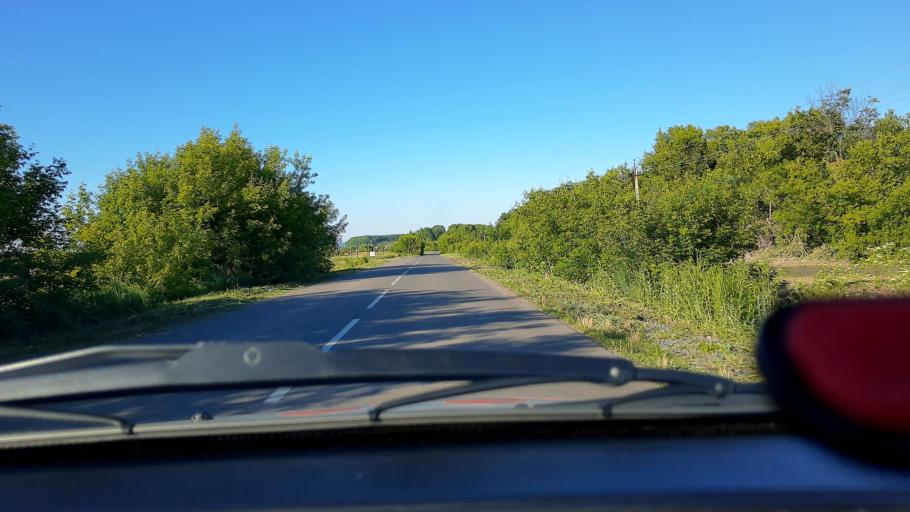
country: RU
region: Bashkortostan
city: Kabakovo
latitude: 54.5098
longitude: 55.9364
